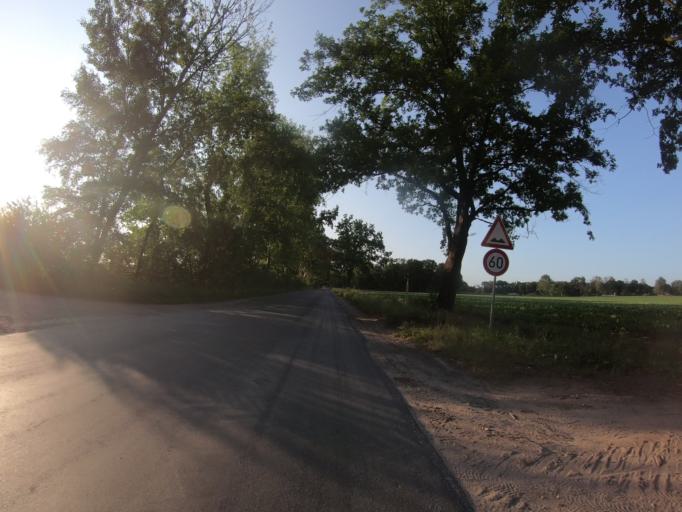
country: DE
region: Lower Saxony
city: Wagenhoff
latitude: 52.5149
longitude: 10.4806
